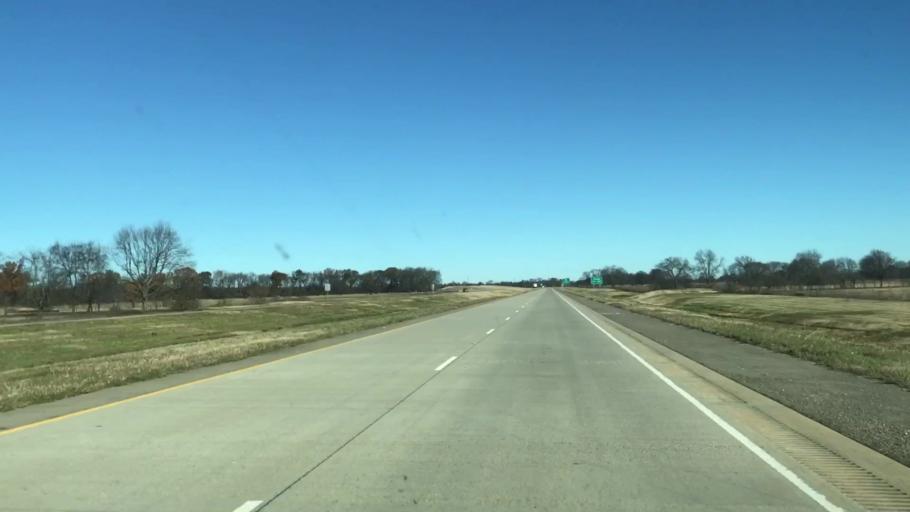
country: US
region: Louisiana
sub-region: Caddo Parish
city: Vivian
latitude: 32.8839
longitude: -93.8602
